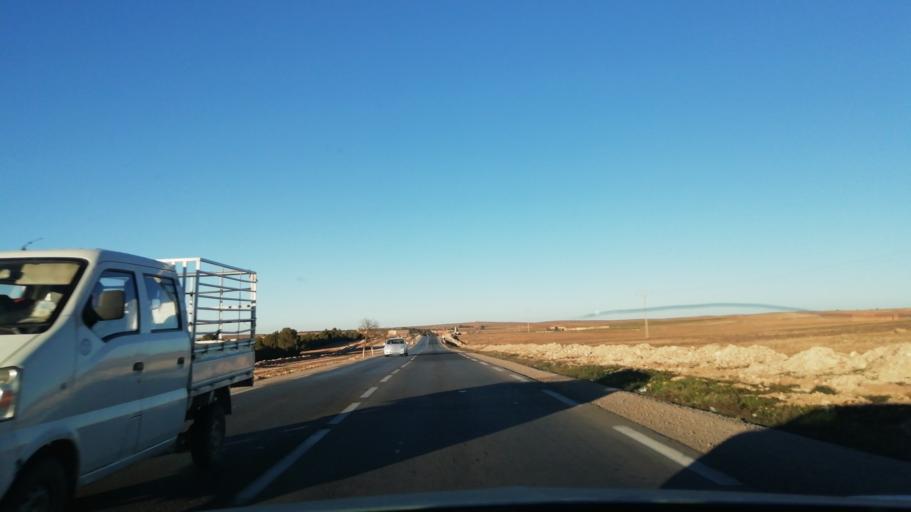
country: DZ
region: Saida
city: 'Ain el Hadjar
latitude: 34.5700
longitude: 0.1240
